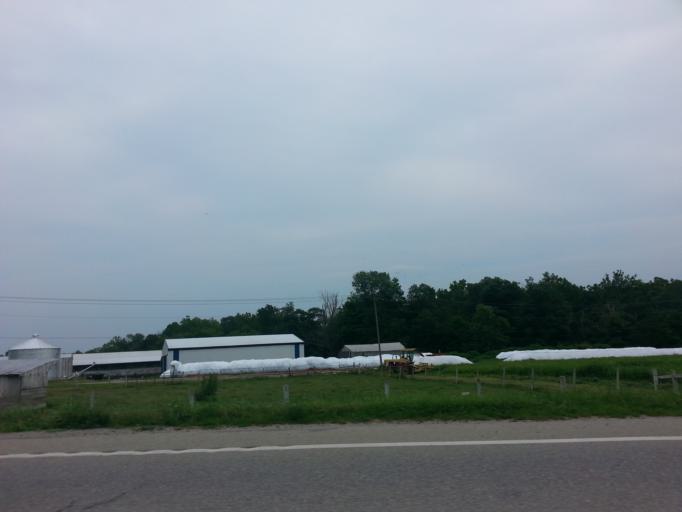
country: US
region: Ohio
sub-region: Brown County
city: Mount Orab
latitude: 38.9713
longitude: -83.9134
